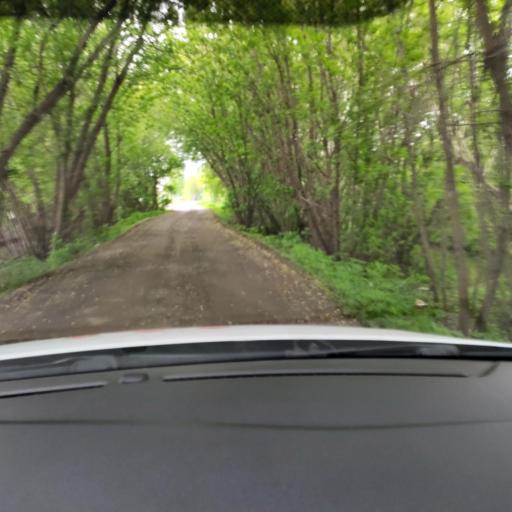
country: RU
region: Tatarstan
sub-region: Gorod Kazan'
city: Kazan
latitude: 55.8119
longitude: 49.2072
